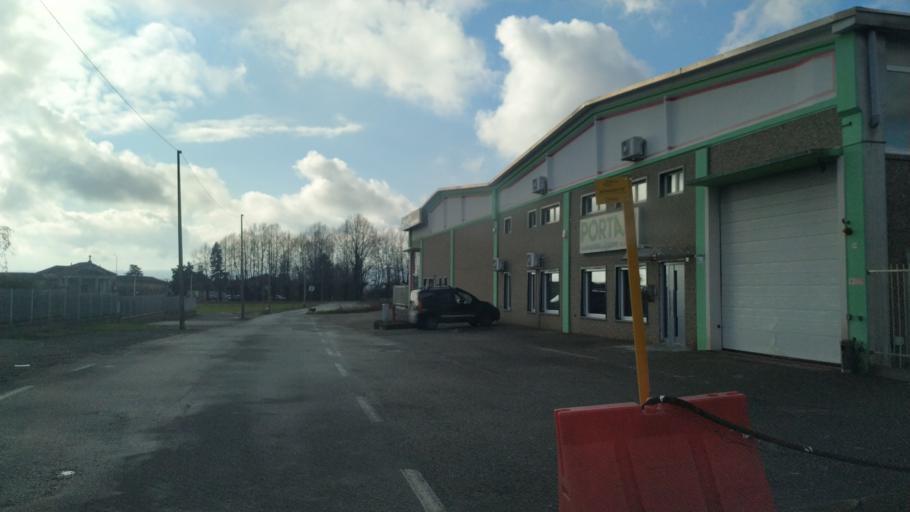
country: IT
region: Piedmont
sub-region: Provincia di Biella
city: Occhieppo Inferiore
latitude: 45.5527
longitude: 8.0383
